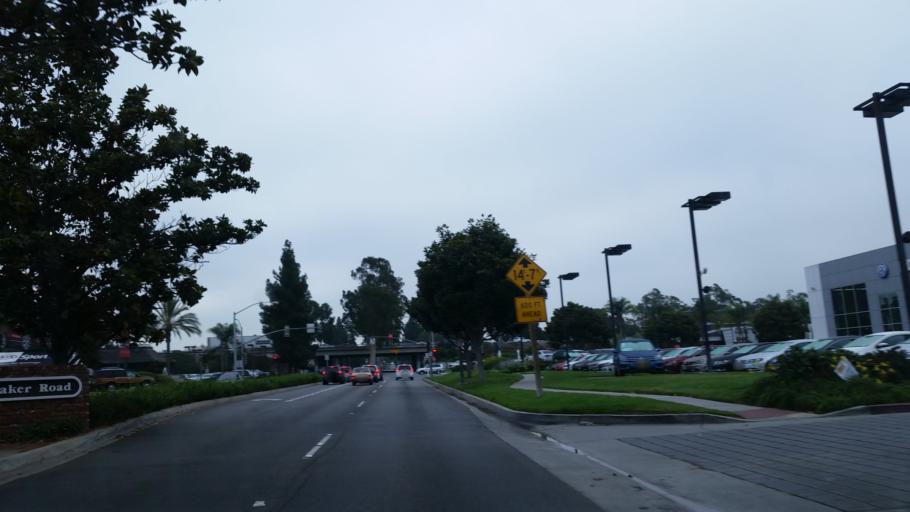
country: US
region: California
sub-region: Los Angeles County
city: Artesia
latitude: 33.8655
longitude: -118.1009
